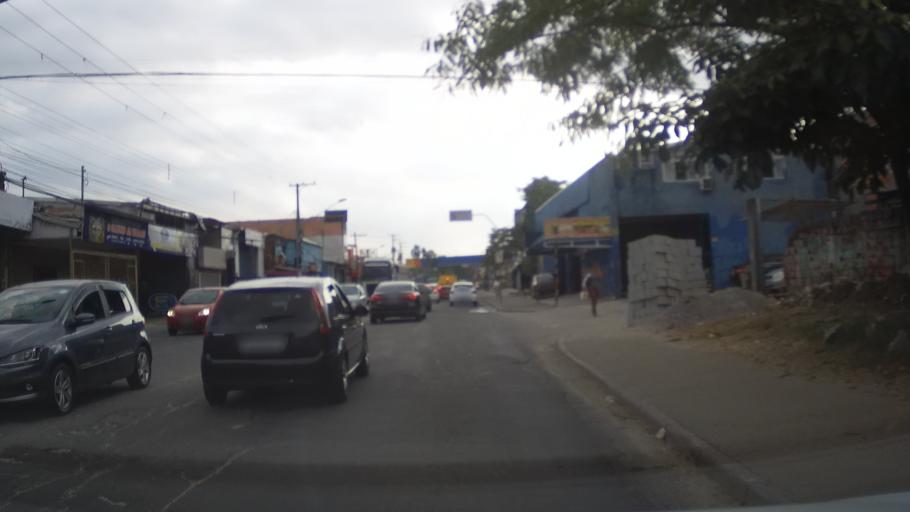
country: BR
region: Sao Paulo
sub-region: Guarulhos
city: Guarulhos
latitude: -23.4248
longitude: -46.4942
